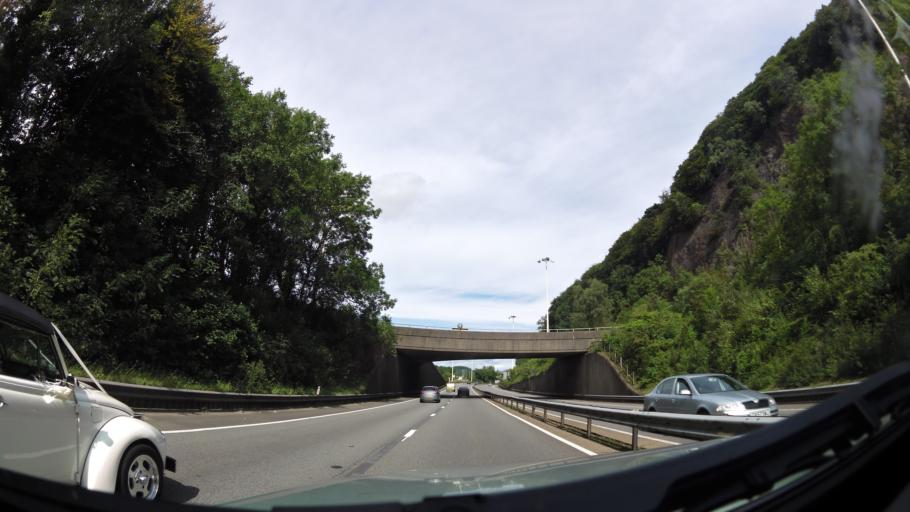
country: GB
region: Wales
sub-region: Cardiff
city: Radyr
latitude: 51.5361
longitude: -3.2590
